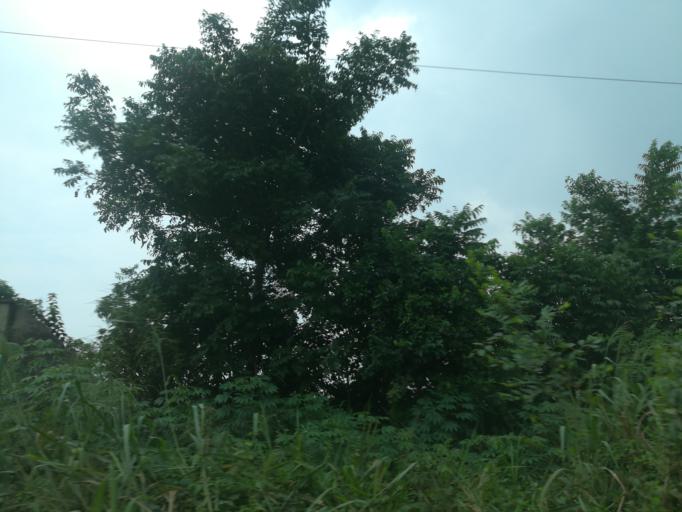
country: NG
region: Lagos
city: Ikorodu
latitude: 6.5798
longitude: 3.5896
